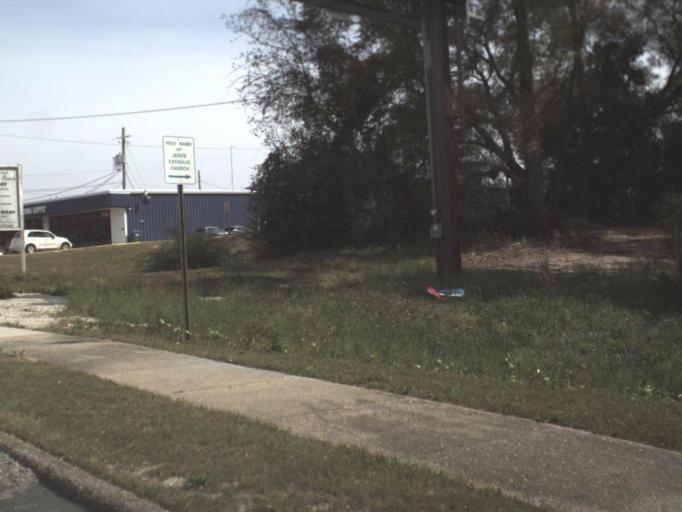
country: US
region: Florida
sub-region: Okaloosa County
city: Niceville
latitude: 30.5180
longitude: -86.4753
